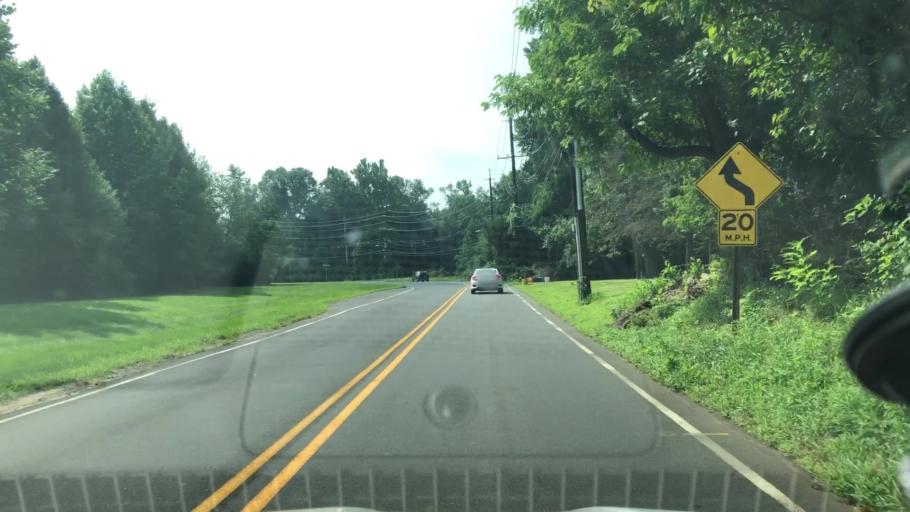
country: US
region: New Jersey
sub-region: Mercer County
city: Lawrenceville
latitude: 40.3065
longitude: -74.6933
